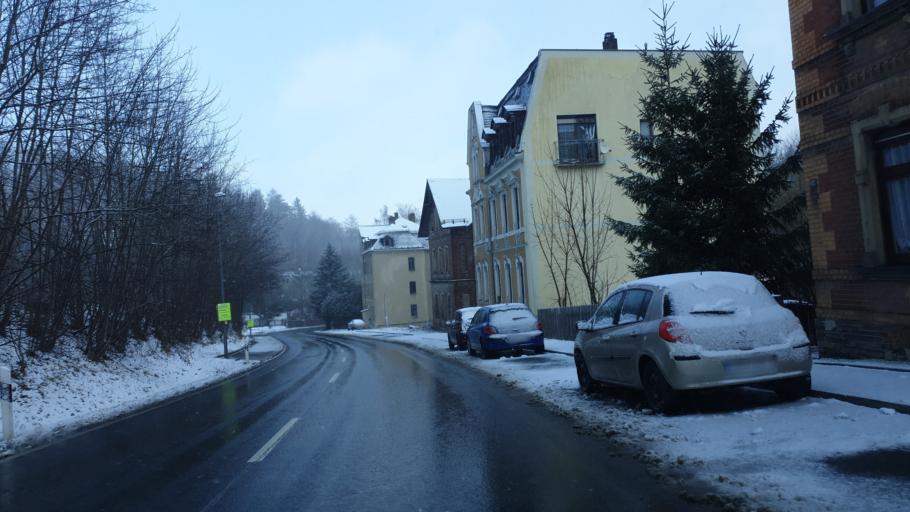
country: DE
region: Saxony
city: Oelsnitz
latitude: 50.4080
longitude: 12.1589
